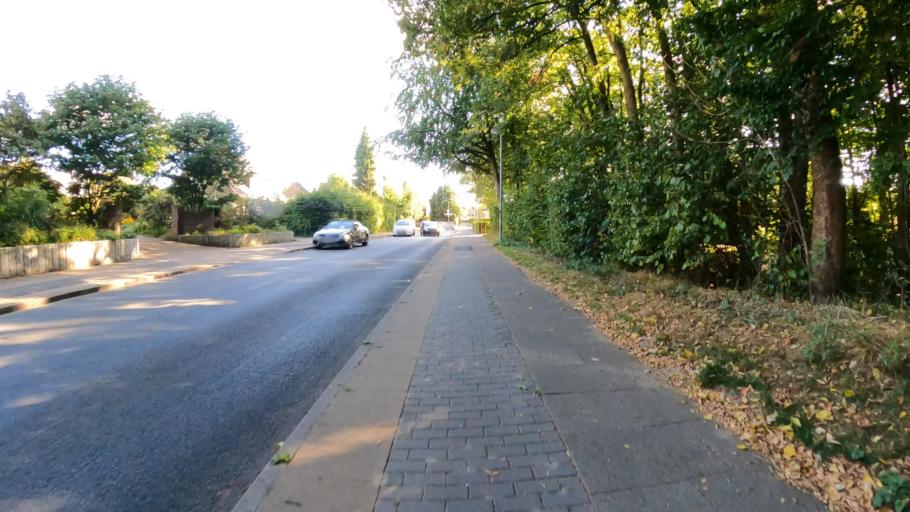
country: DE
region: Schleswig-Holstein
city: Ahrensburg
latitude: 53.6589
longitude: 10.2428
